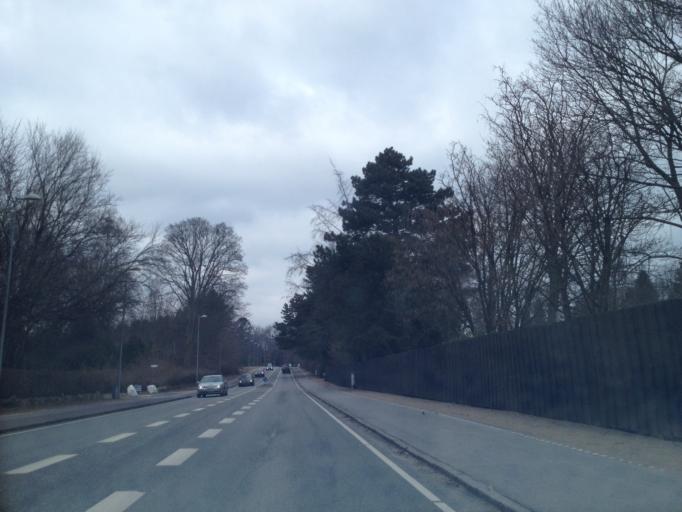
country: DK
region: Capital Region
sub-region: Rudersdal Kommune
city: Trorod
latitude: 55.8653
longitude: 12.5527
